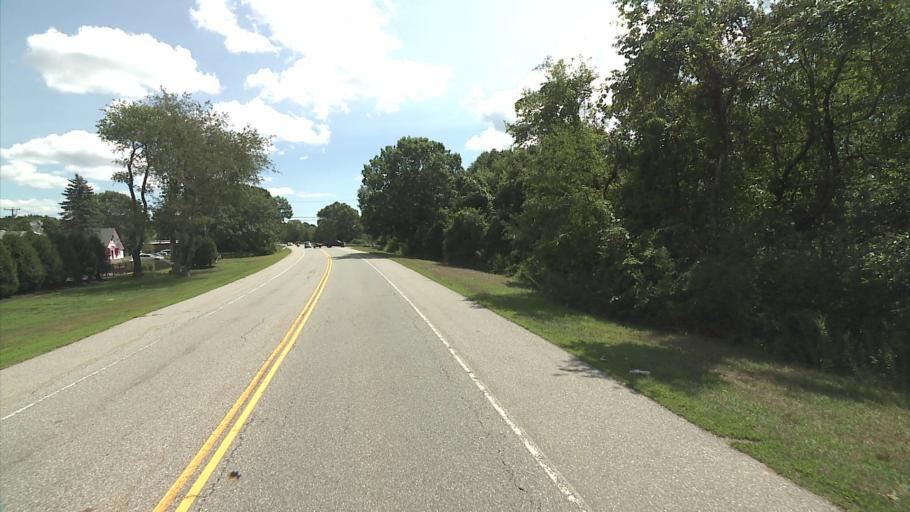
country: US
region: Connecticut
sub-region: New London County
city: Mystic
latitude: 41.3433
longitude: -71.9496
